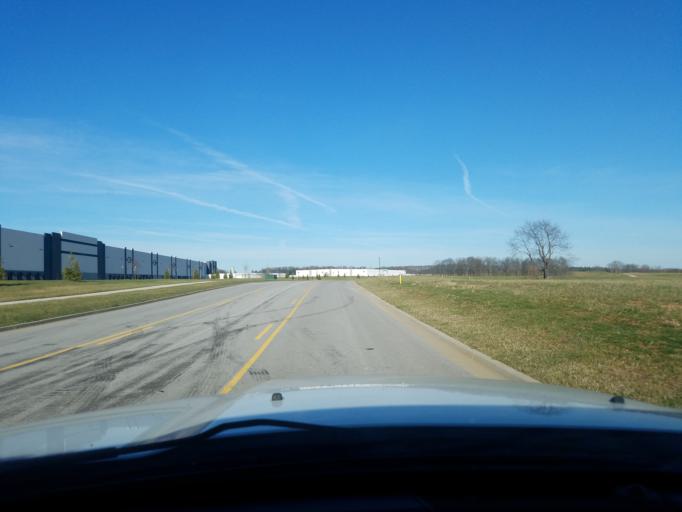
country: US
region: Indiana
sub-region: Clark County
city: Charlestown
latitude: 38.3845
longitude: -85.6771
